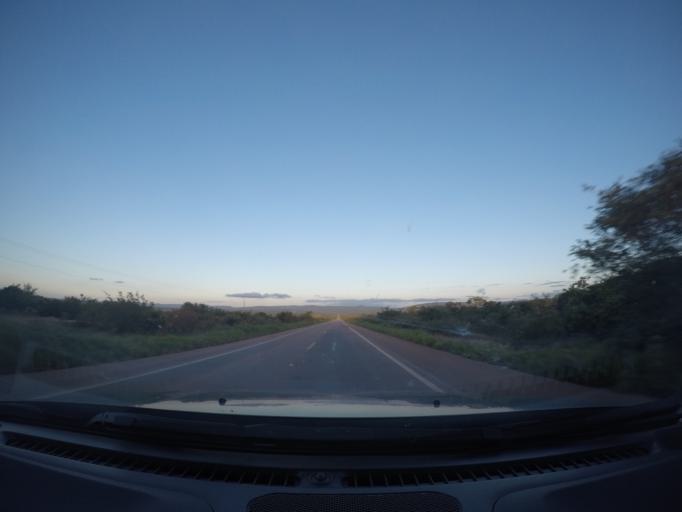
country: BR
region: Bahia
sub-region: Seabra
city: Seabra
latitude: -12.4093
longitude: -41.9664
